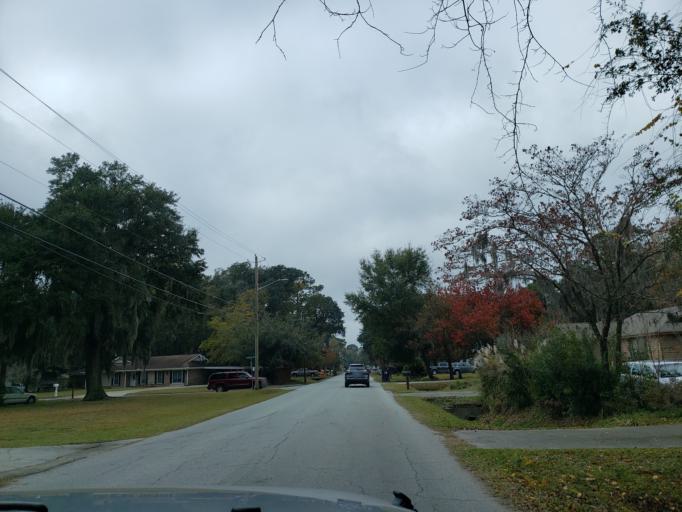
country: US
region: Georgia
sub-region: Chatham County
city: Wilmington Island
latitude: 32.0109
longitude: -80.9679
